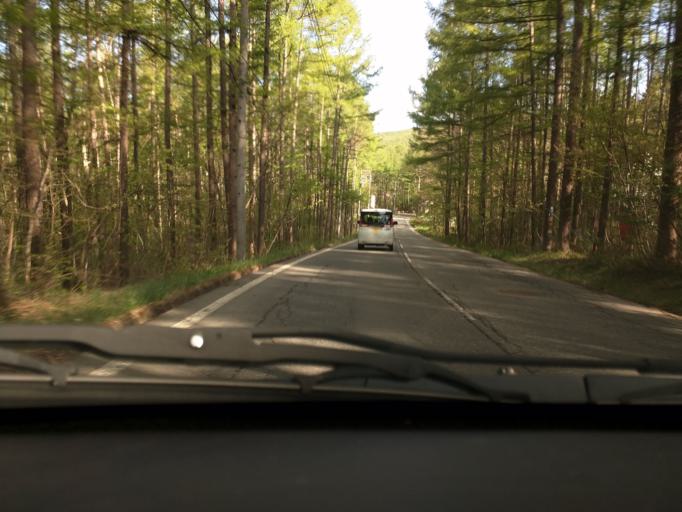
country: JP
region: Nagano
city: Nagano-shi
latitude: 36.7119
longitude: 138.1153
